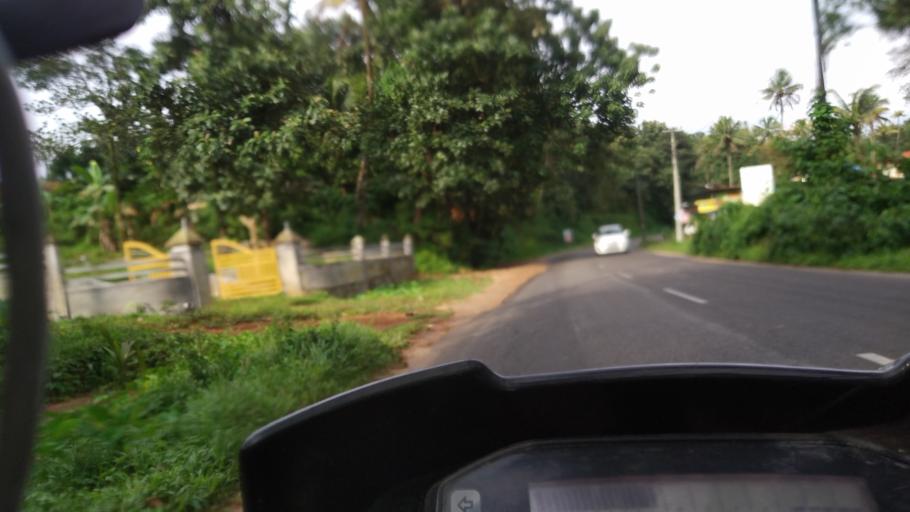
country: IN
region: Kerala
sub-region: Ernakulam
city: Kotamangalam
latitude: 10.0498
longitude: 76.7226
